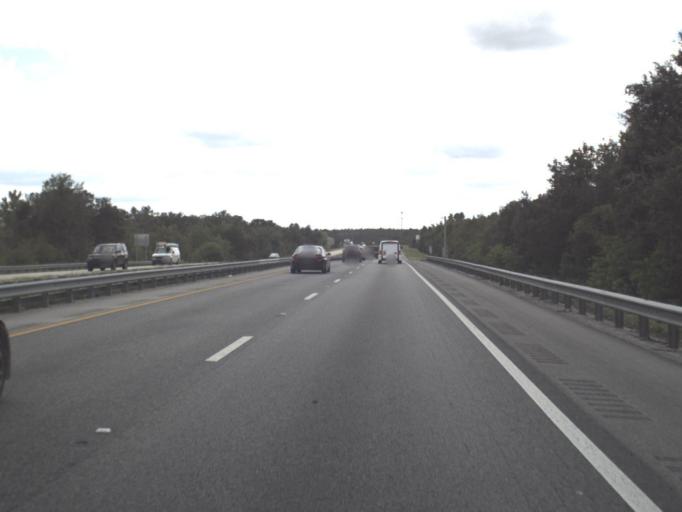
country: US
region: Florida
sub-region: Osceola County
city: Saint Cloud
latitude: 28.2351
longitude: -81.3247
